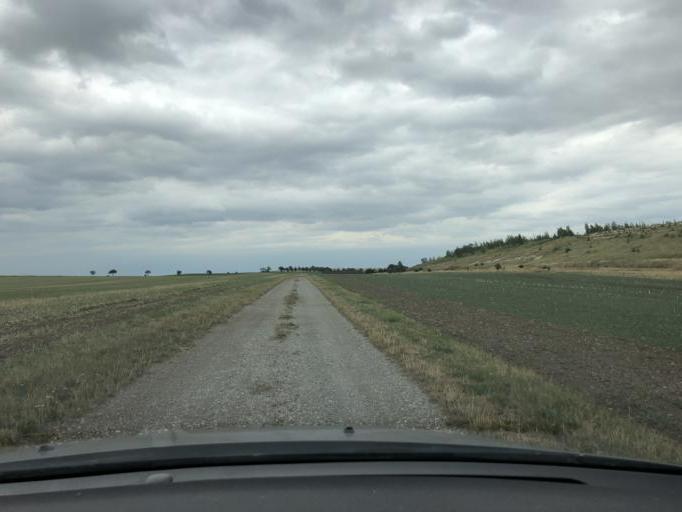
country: DE
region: Saxony-Anhalt
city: Nienburg/Saale
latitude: 51.8312
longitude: 11.7954
